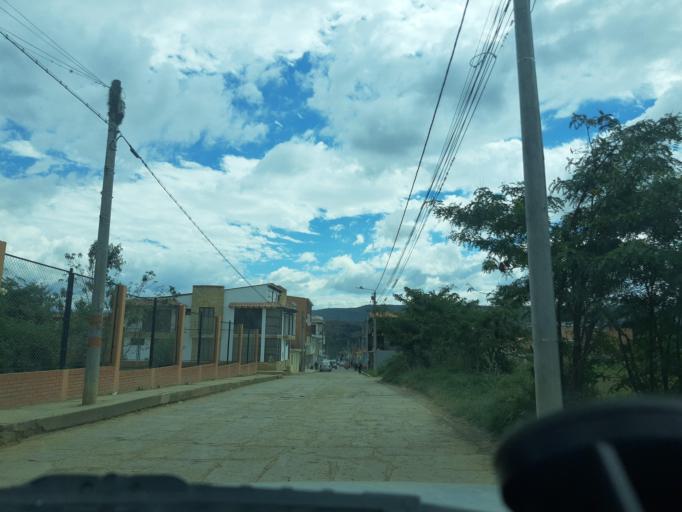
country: CO
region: Boyaca
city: Sutamarchan
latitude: 5.6214
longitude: -73.6226
